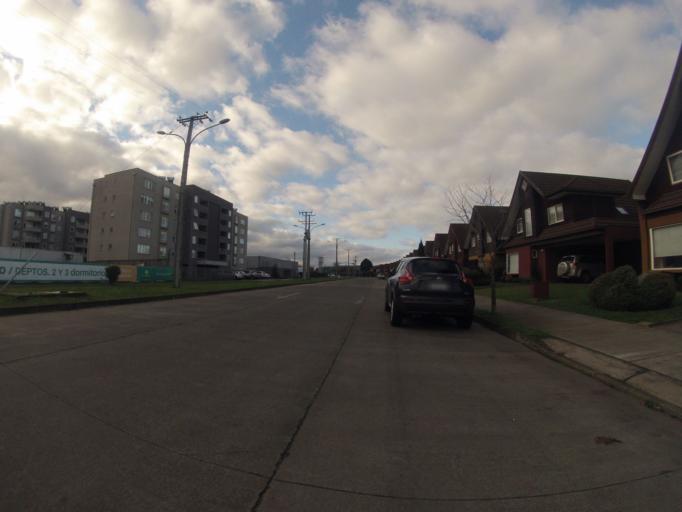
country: CL
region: Araucania
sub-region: Provincia de Cautin
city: Temuco
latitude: -38.7422
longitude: -72.6434
